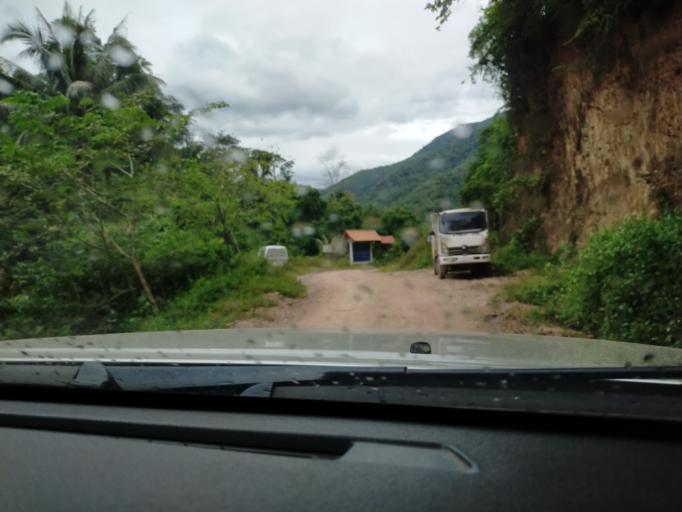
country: TH
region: Nan
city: Chaloem Phra Kiat
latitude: 19.8167
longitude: 101.3586
